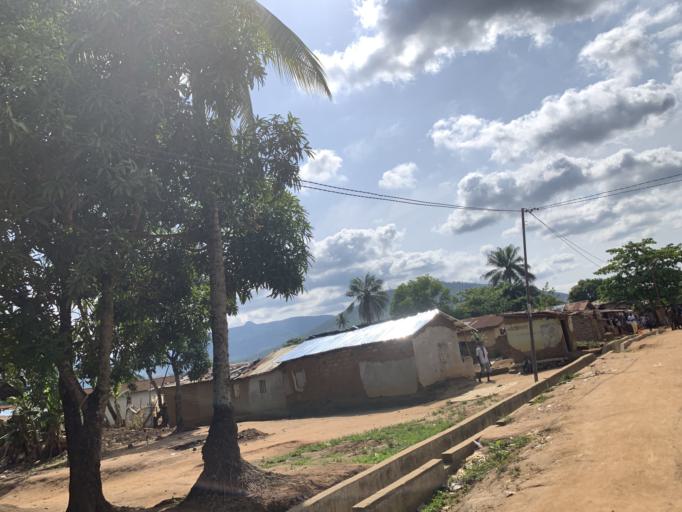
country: SL
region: Western Area
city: Waterloo
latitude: 8.3302
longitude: -13.0632
